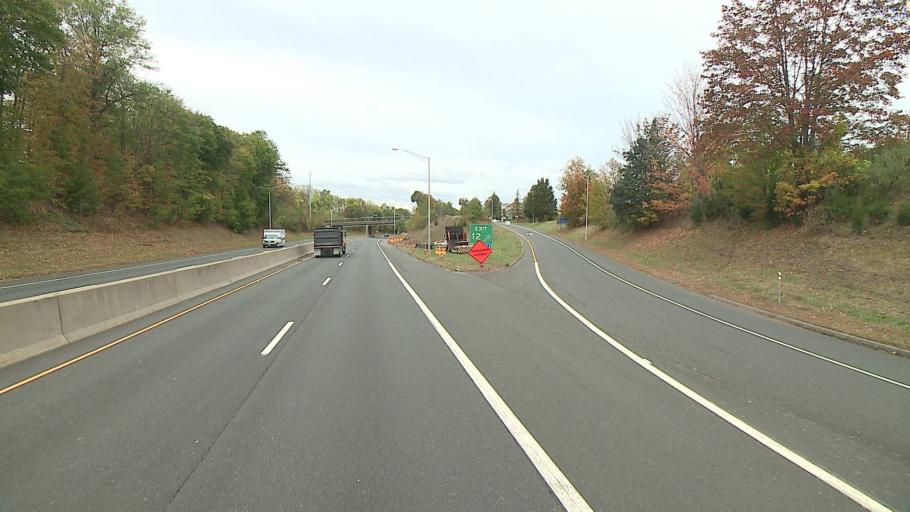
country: US
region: Connecticut
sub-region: Middlesex County
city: Middletown
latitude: 41.5456
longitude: -72.6294
